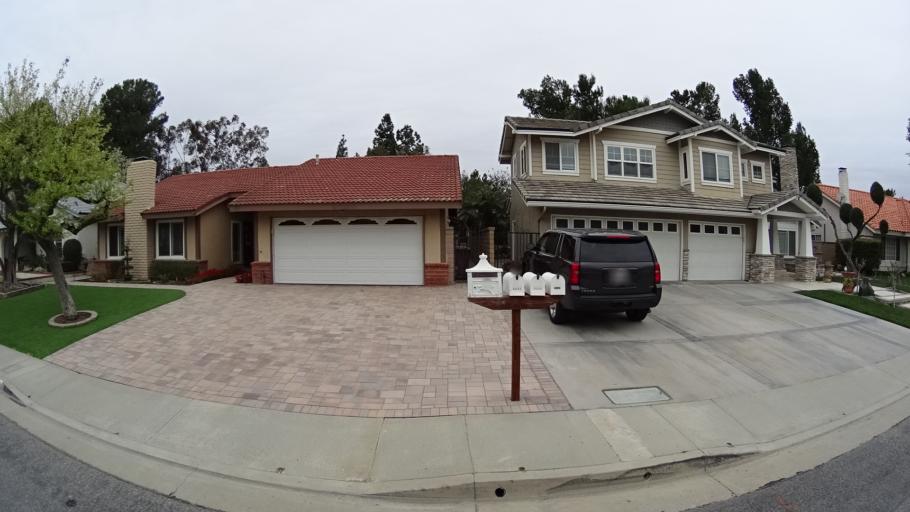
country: US
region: California
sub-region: Orange County
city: Villa Park
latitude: 33.8403
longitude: -117.7453
